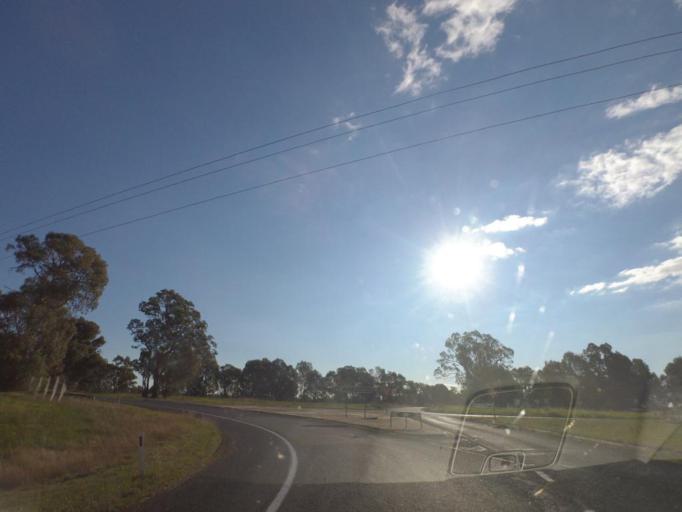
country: AU
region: Victoria
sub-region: Benalla
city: Benalla
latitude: -36.6965
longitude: 145.6577
